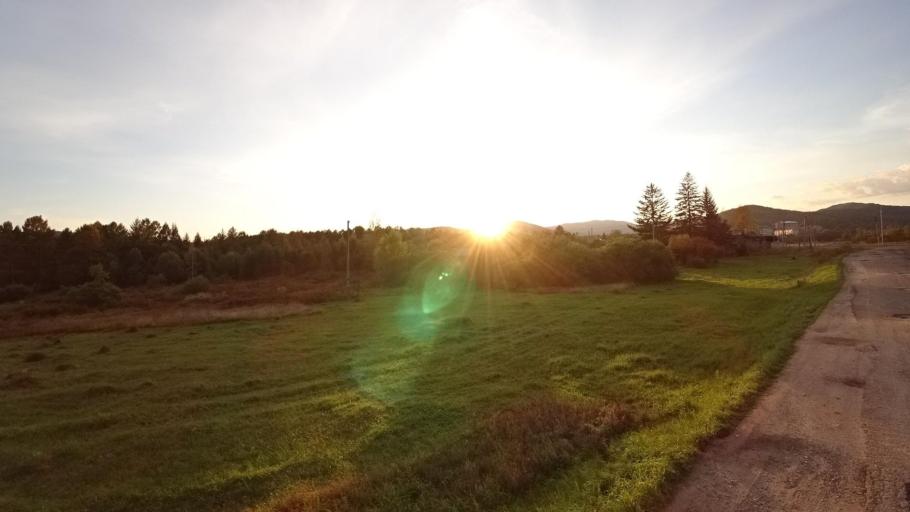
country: RU
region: Jewish Autonomous Oblast
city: Kul'dur
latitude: 49.1981
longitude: 131.6331
